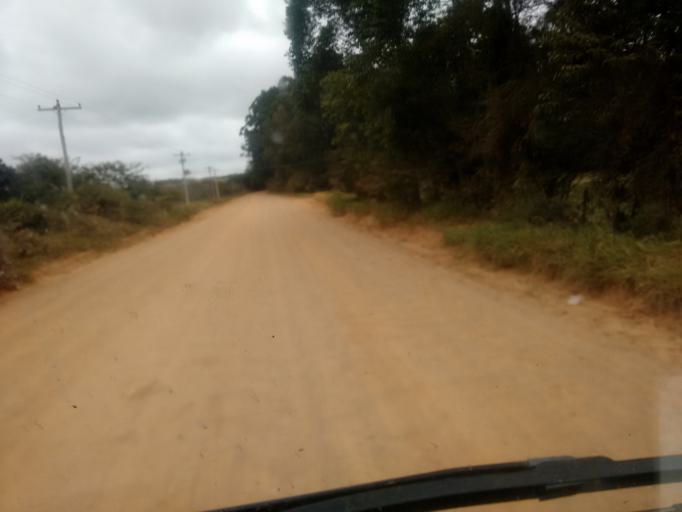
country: BR
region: Rio Grande do Sul
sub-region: Camaqua
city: Camaqua
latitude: -30.8148
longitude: -51.8161
